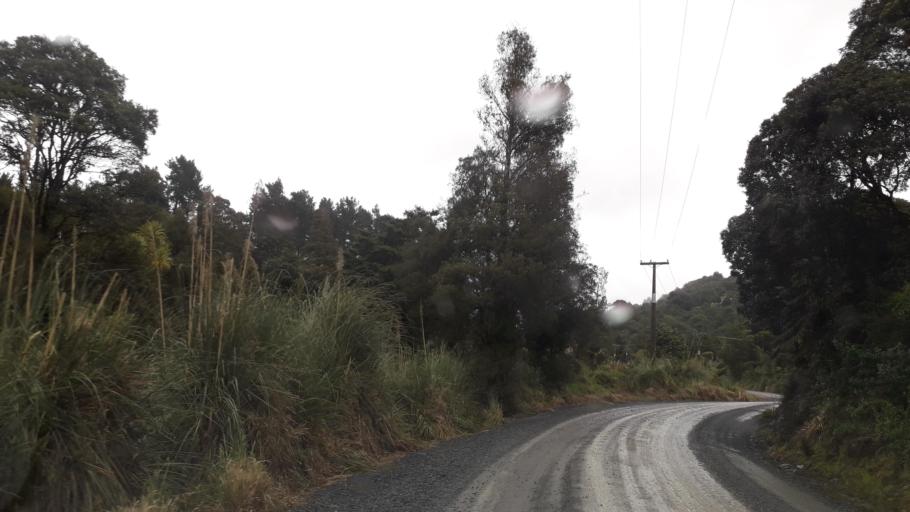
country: NZ
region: Northland
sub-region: Far North District
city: Kerikeri
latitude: -35.1171
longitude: 173.7526
